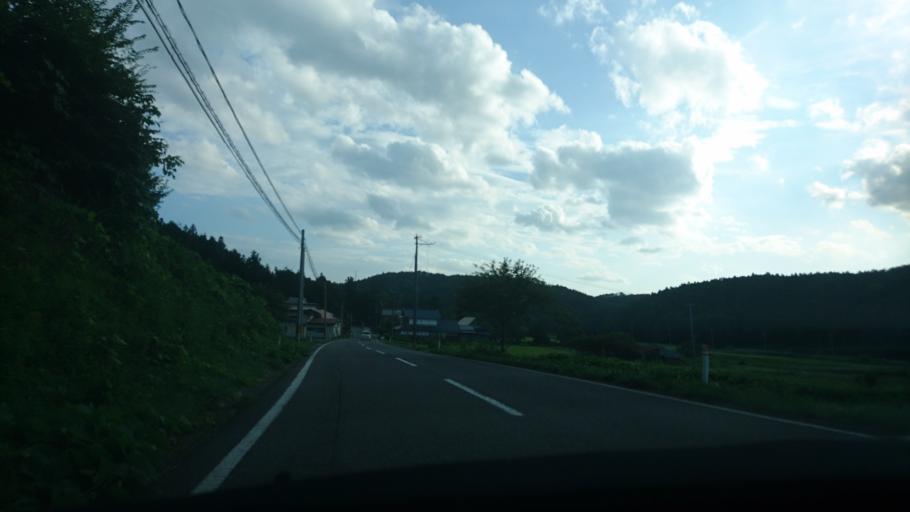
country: JP
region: Iwate
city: Ichinoseki
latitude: 39.0212
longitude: 141.2906
